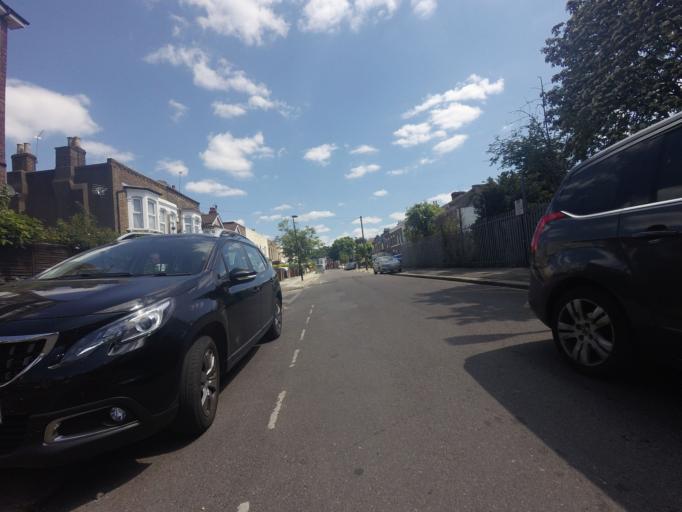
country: GB
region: England
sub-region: Greater London
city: East Ham
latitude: 51.5503
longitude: 0.0082
